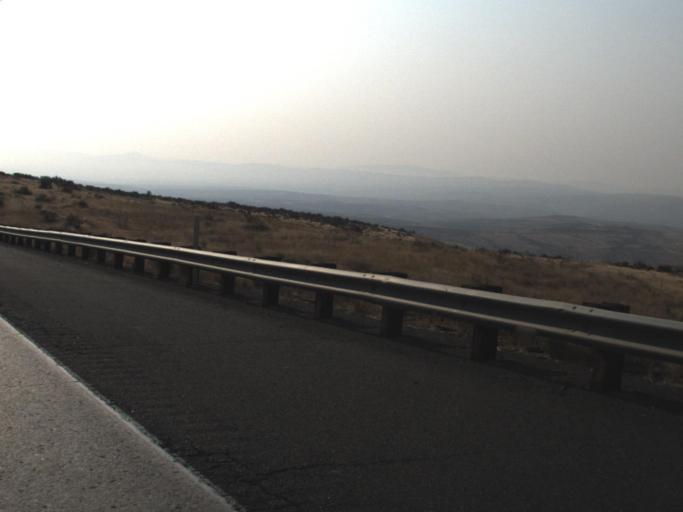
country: US
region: Washington
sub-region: Kittitas County
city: Kittitas
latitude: 46.8697
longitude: -120.4167
